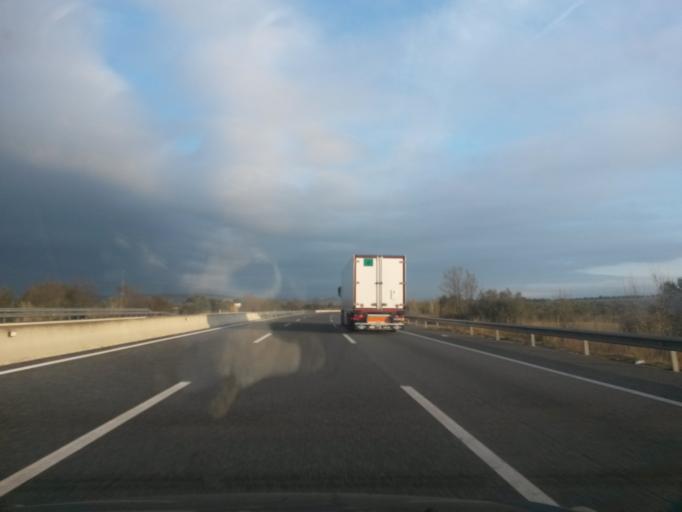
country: ES
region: Catalonia
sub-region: Provincia de Girona
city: Vilafant
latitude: 42.2348
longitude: 2.9368
